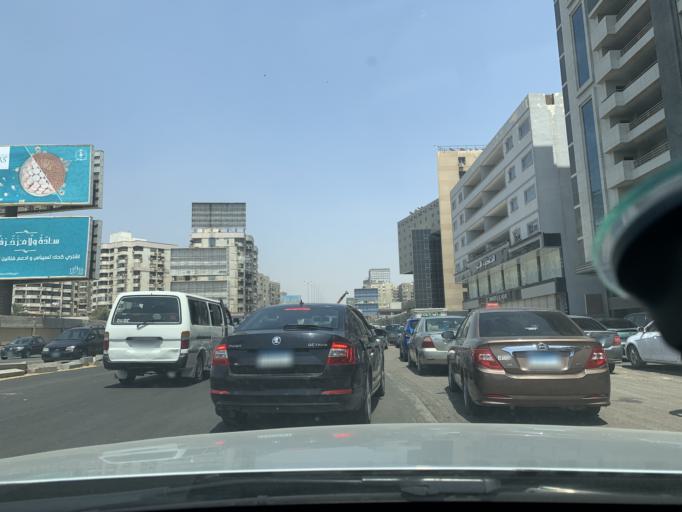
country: EG
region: Muhafazat al Qahirah
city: Cairo
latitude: 30.0681
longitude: 31.3344
